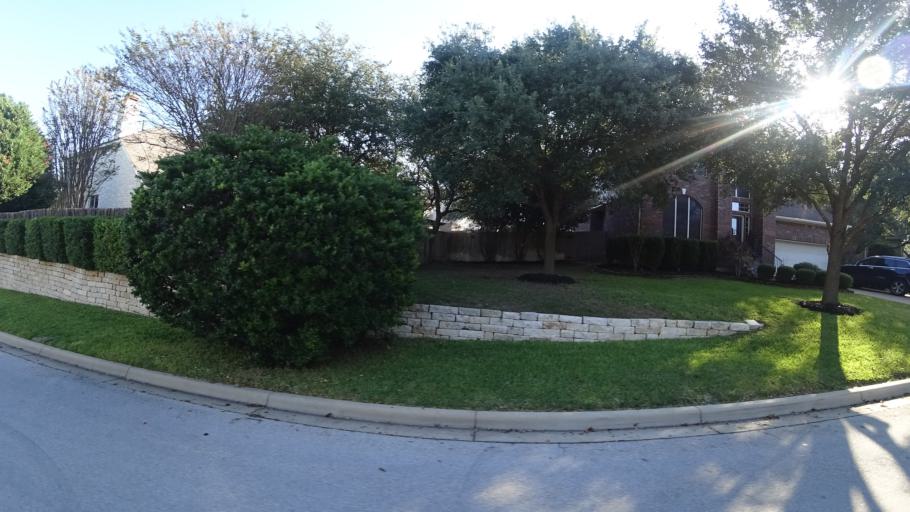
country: US
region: Texas
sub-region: Travis County
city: Hudson Bend
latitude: 30.3715
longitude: -97.9001
